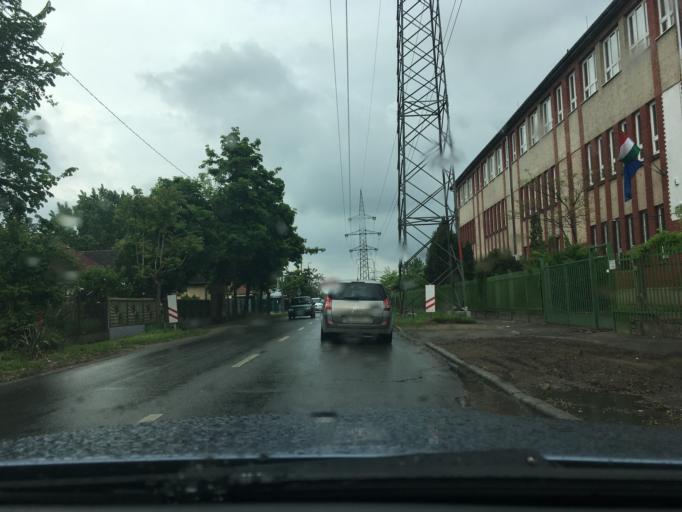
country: HU
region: Hajdu-Bihar
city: Debrecen
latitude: 47.5288
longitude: 21.6602
